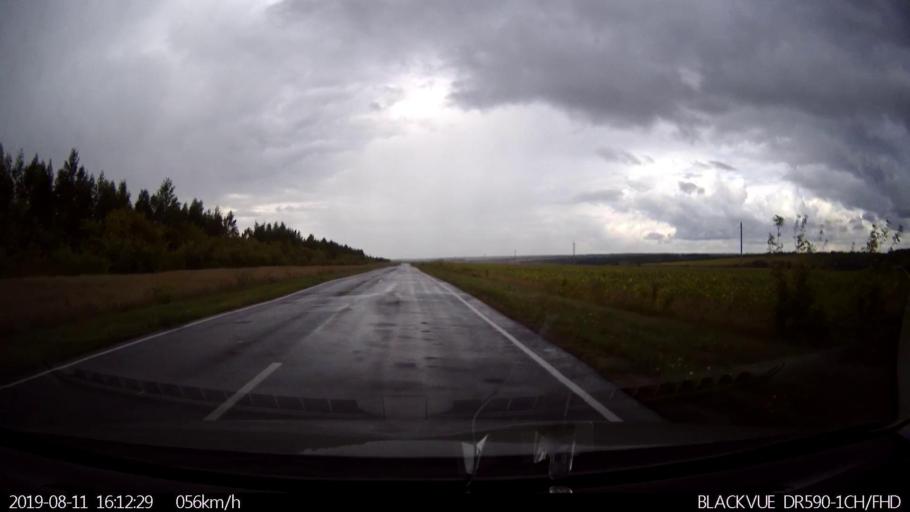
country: RU
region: Ulyanovsk
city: Ignatovka
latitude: 54.0118
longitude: 47.6403
